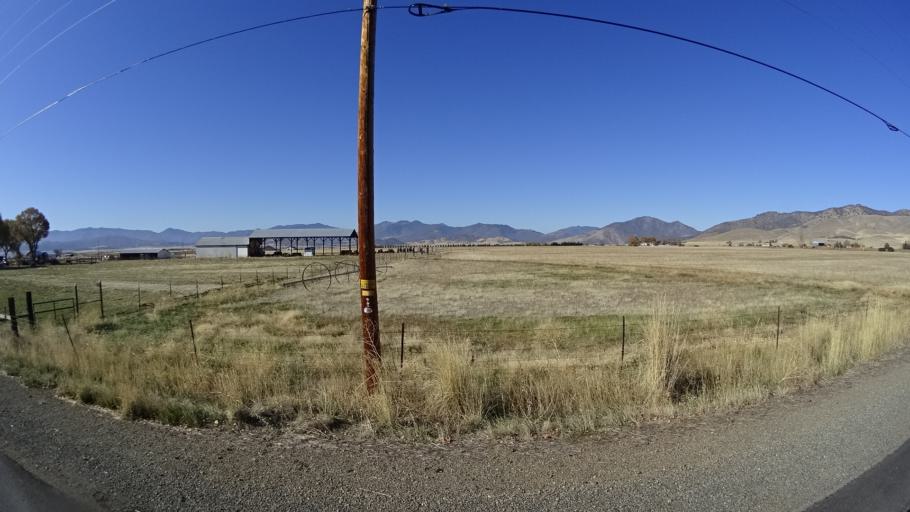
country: US
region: California
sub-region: Siskiyou County
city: Montague
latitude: 41.7582
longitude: -122.5247
